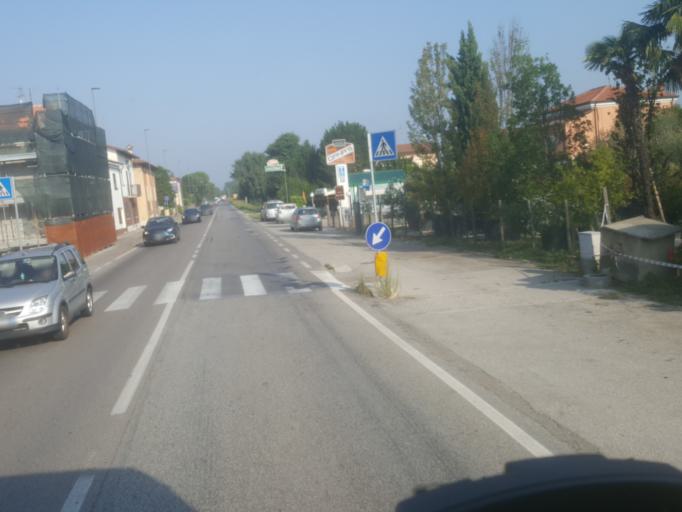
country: IT
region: Emilia-Romagna
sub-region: Provincia di Ravenna
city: Mezzano
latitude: 44.4590
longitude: 12.1003
